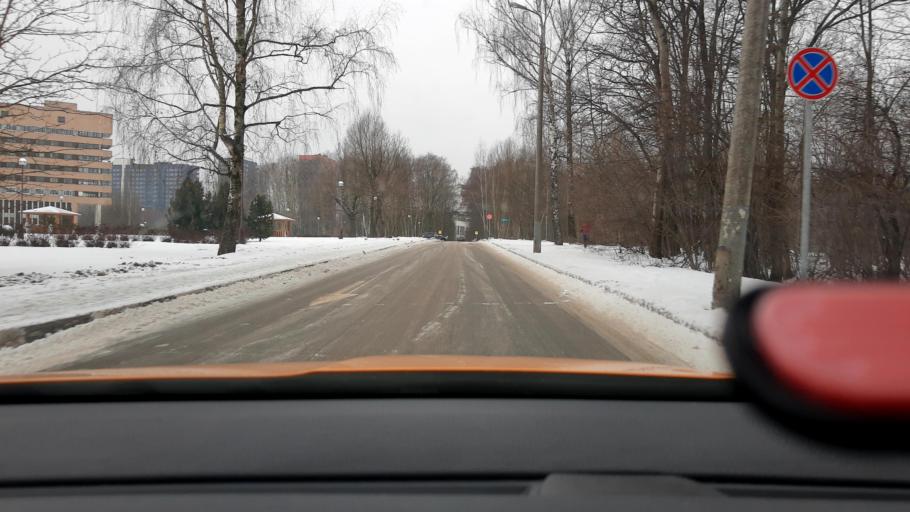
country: RU
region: Moskovskaya
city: Krasnogorsk
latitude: 55.8755
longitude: 37.3241
